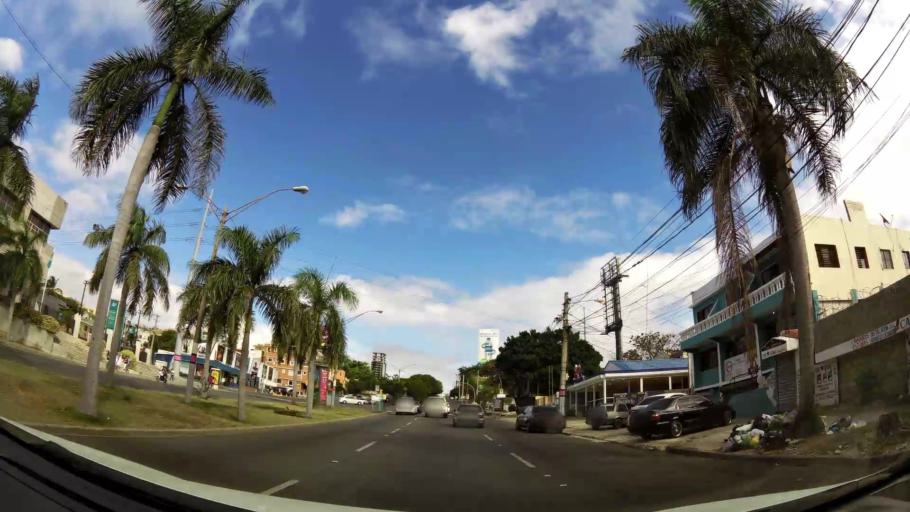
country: DO
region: Nacional
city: La Julia
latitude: 18.4545
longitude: -69.9297
